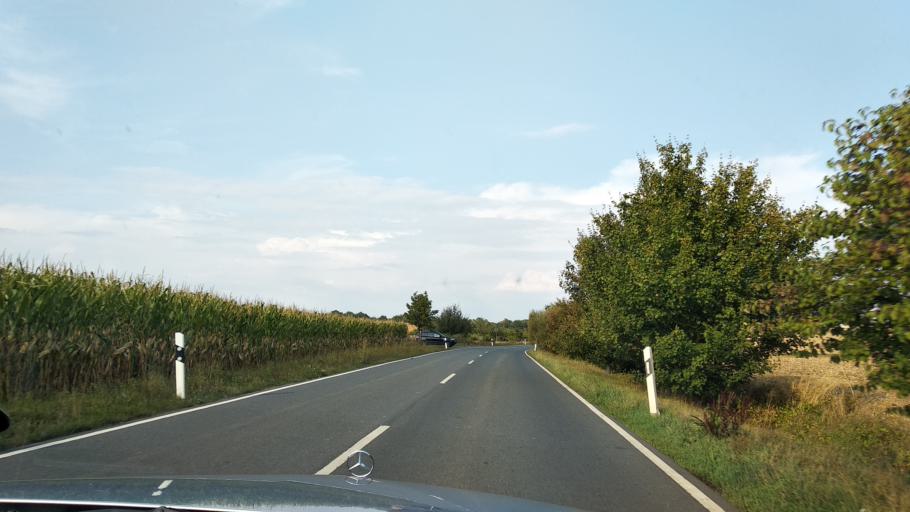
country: DE
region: Baden-Wuerttemberg
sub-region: Karlsruhe Region
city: Walldurn
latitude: 49.5909
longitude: 9.3955
